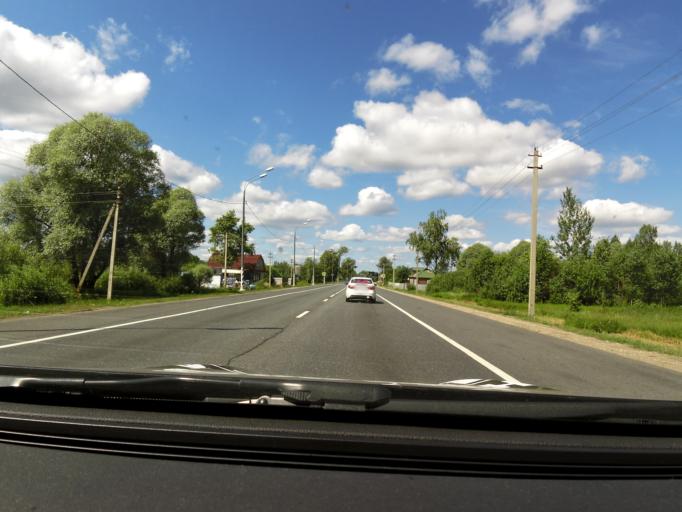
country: RU
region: Tverskaya
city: Kuzhenkino
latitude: 57.7270
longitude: 34.0668
